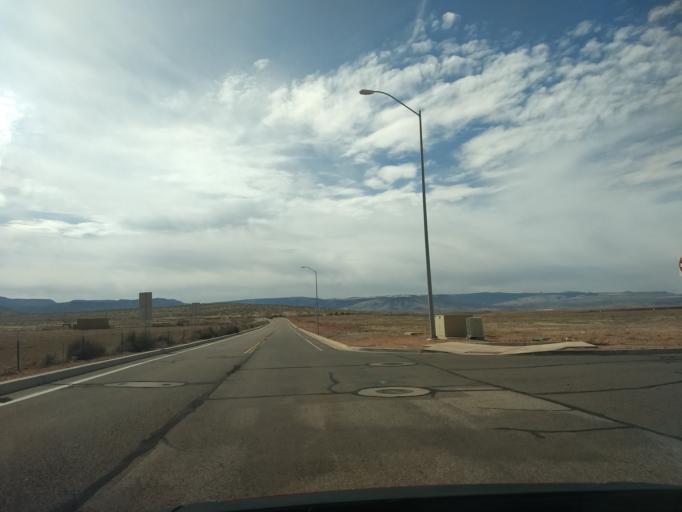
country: US
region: Utah
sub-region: Washington County
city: Washington
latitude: 37.0286
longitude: -113.5064
